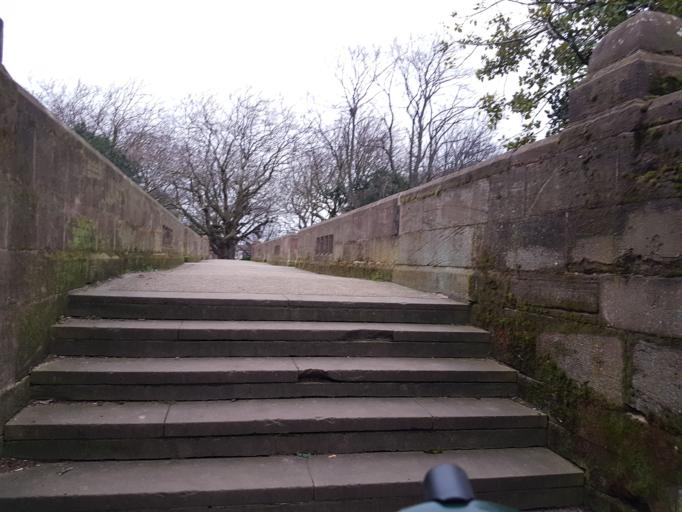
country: GB
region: England
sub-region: Liverpool
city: Liverpool
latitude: 53.4364
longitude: -2.9660
